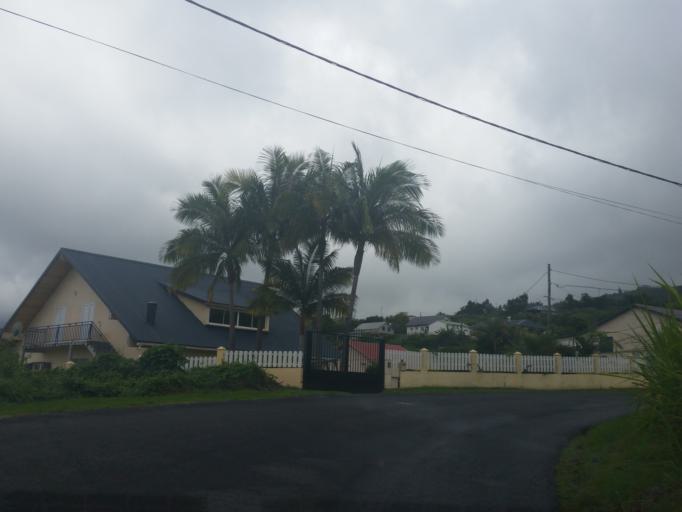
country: RE
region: Reunion
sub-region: Reunion
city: Le Tampon
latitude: -21.2399
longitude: 55.5170
